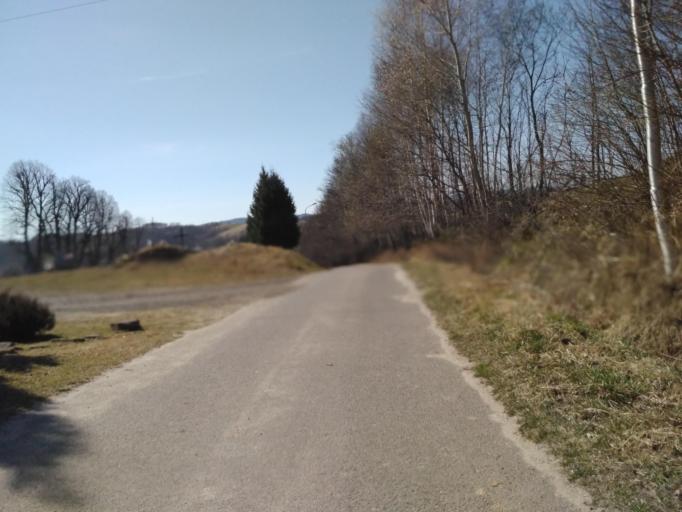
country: PL
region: Subcarpathian Voivodeship
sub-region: Powiat brzozowski
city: Blizne
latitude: 49.7534
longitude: 21.9791
